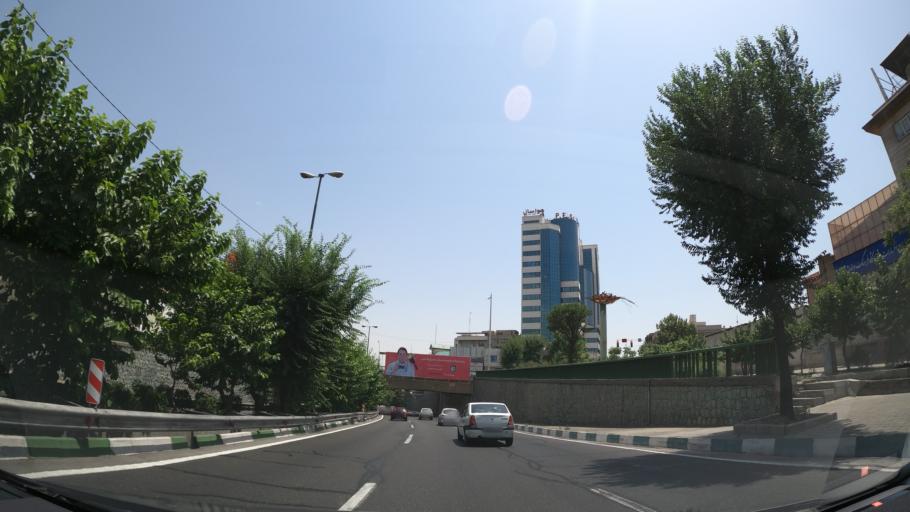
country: IR
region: Tehran
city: Tehran
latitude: 35.7299
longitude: 51.4209
